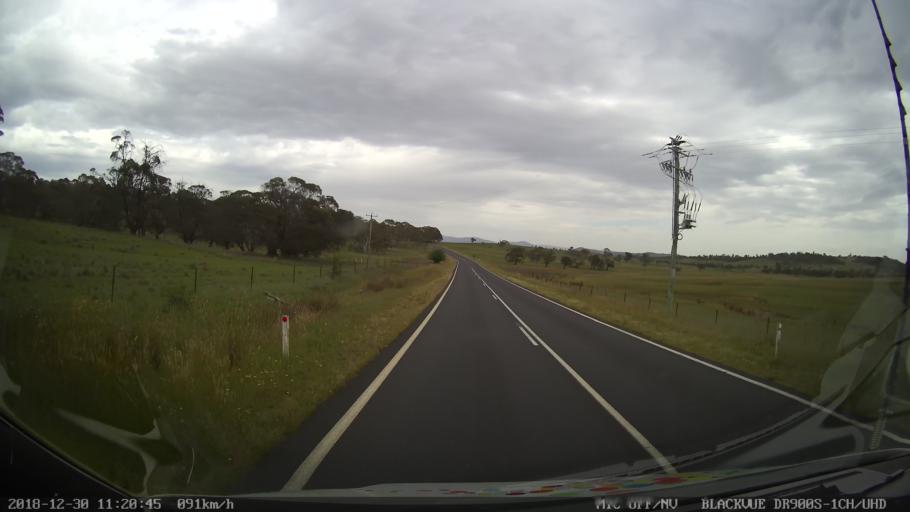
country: AU
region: New South Wales
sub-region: Snowy River
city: Jindabyne
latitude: -36.5145
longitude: 148.6875
